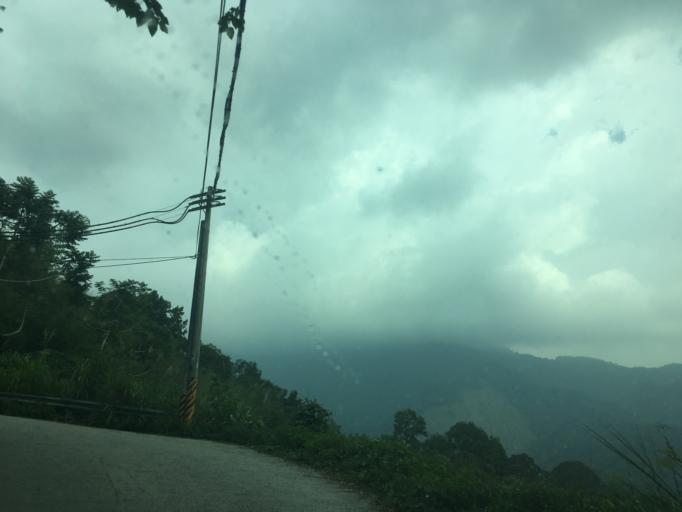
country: TW
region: Taiwan
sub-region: Miaoli
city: Miaoli
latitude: 24.3906
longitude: 120.9758
